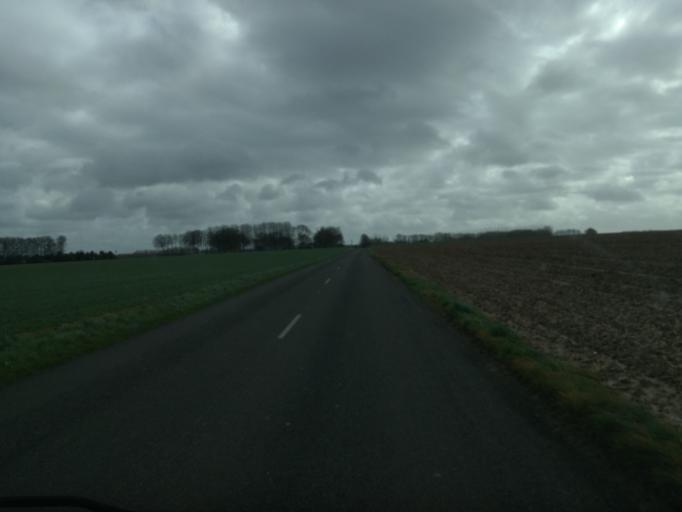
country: FR
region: Haute-Normandie
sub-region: Departement de la Seine-Maritime
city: Yebleron
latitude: 49.6600
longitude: 0.5142
